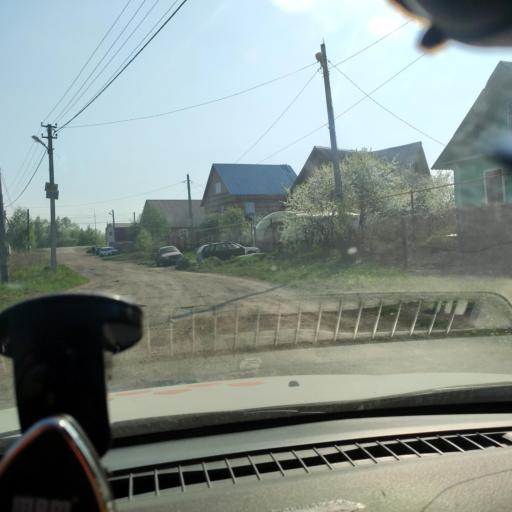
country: RU
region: Bashkortostan
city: Iglino
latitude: 54.7957
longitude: 56.2659
